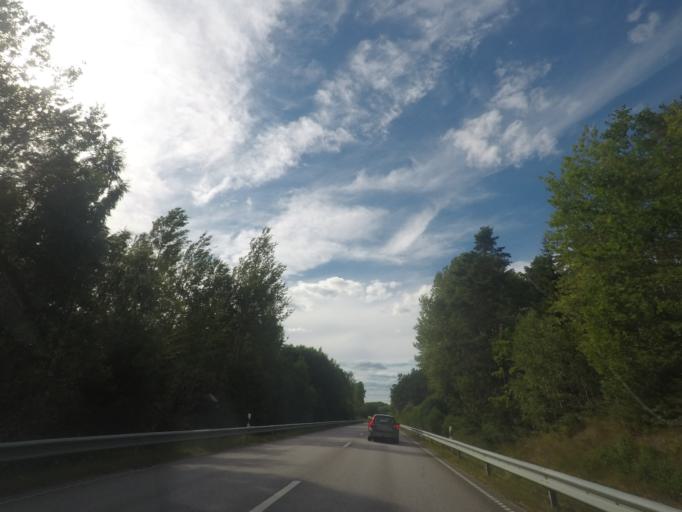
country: SE
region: Stockholm
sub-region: Norrtalje Kommun
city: Skanninge
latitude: 59.8976
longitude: 18.6128
